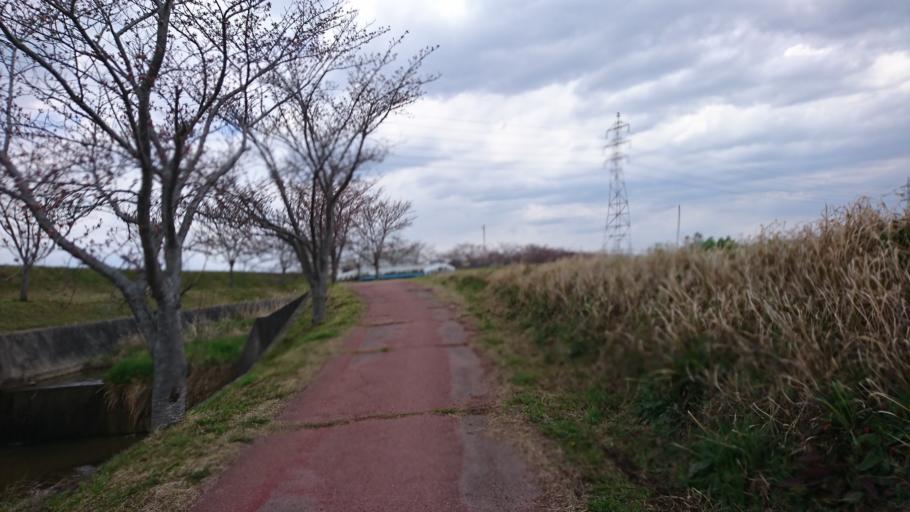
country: JP
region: Hyogo
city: Kakogawacho-honmachi
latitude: 34.7559
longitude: 134.9098
